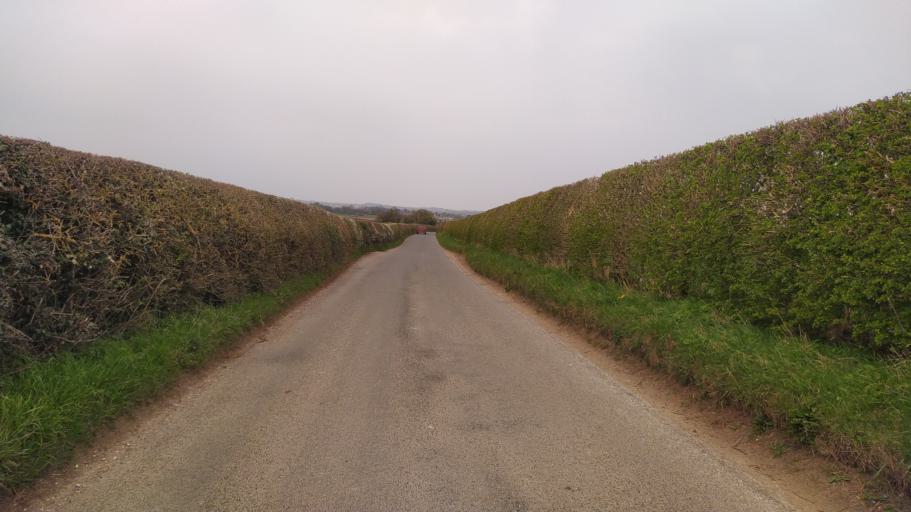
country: GB
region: England
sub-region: Wiltshire
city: Bower Chalke
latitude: 50.9417
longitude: -2.0018
